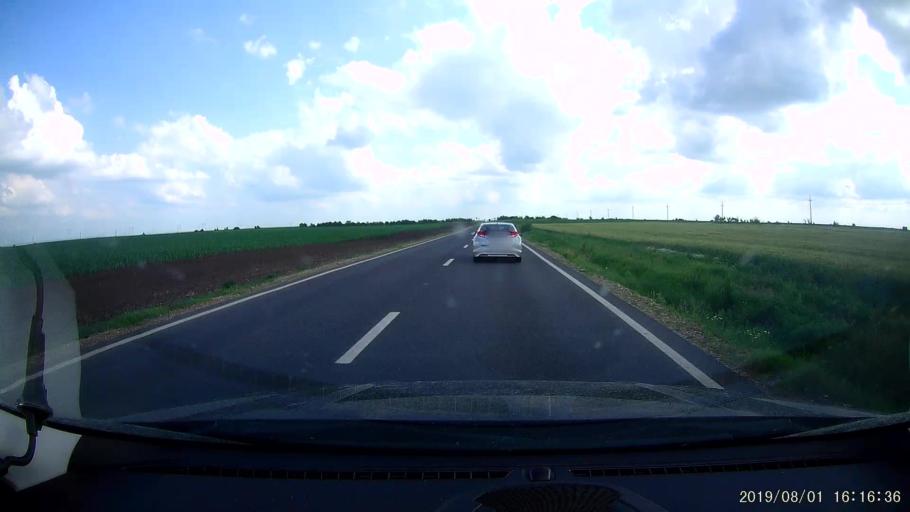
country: RO
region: Calarasi
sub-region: Comuna Stefan Voda
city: Stefan Voda
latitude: 44.3173
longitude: 27.3574
